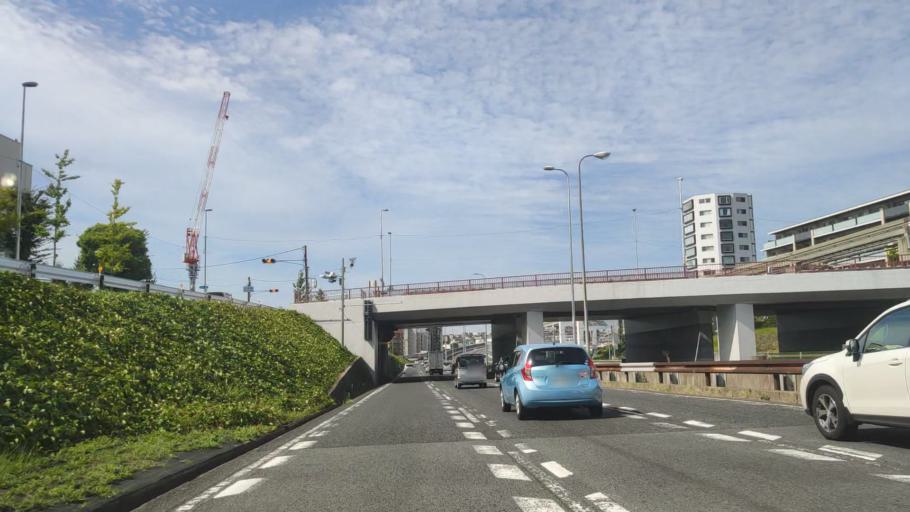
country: JP
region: Osaka
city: Toyonaka
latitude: 34.8022
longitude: 135.4722
